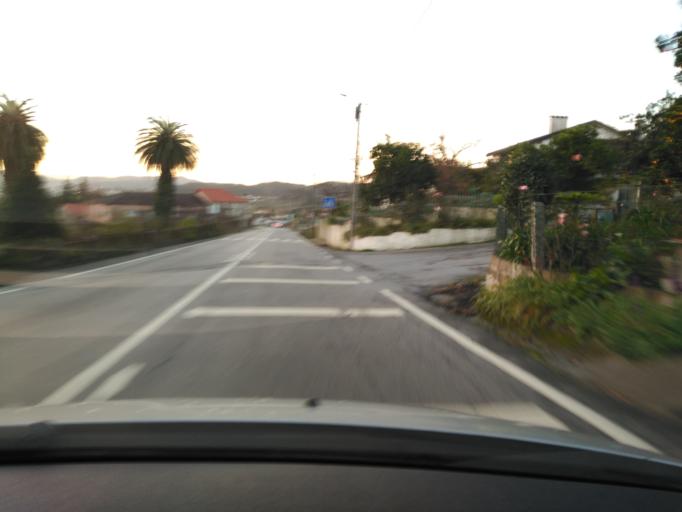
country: PT
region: Braga
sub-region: Guimaraes
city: Brito
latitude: 41.5001
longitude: -8.3649
